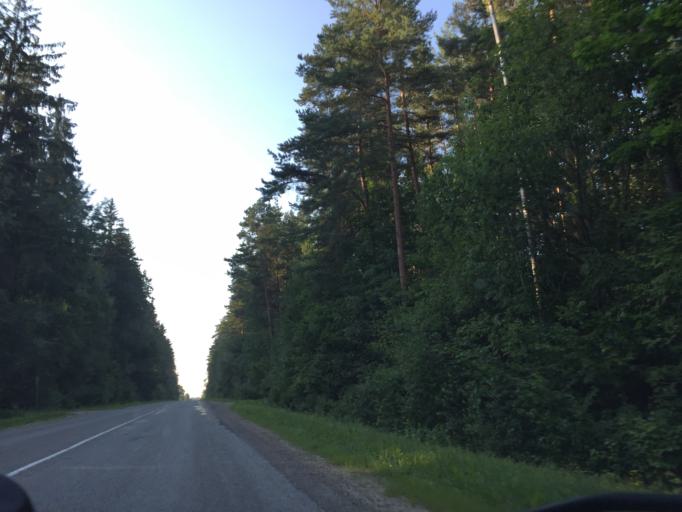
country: LV
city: Tervete
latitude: 56.4623
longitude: 23.4045
